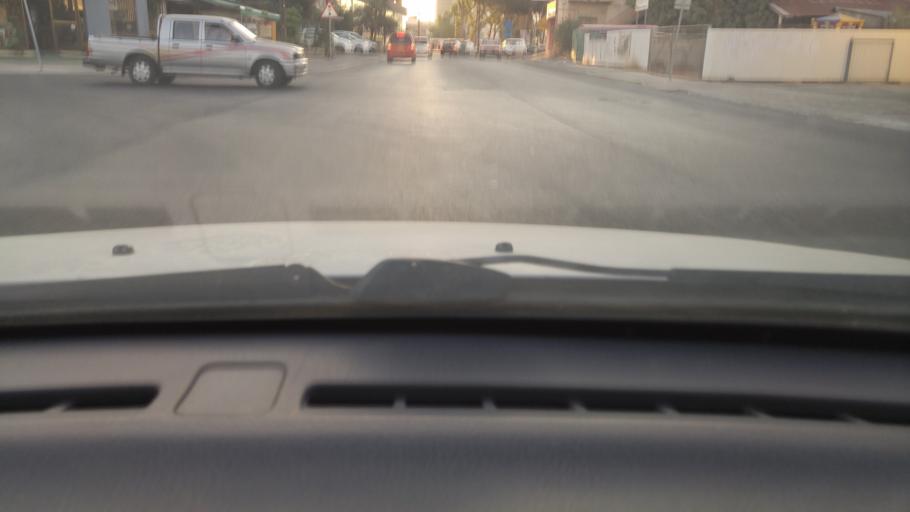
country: CY
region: Limassol
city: Limassol
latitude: 34.6734
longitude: 33.0190
